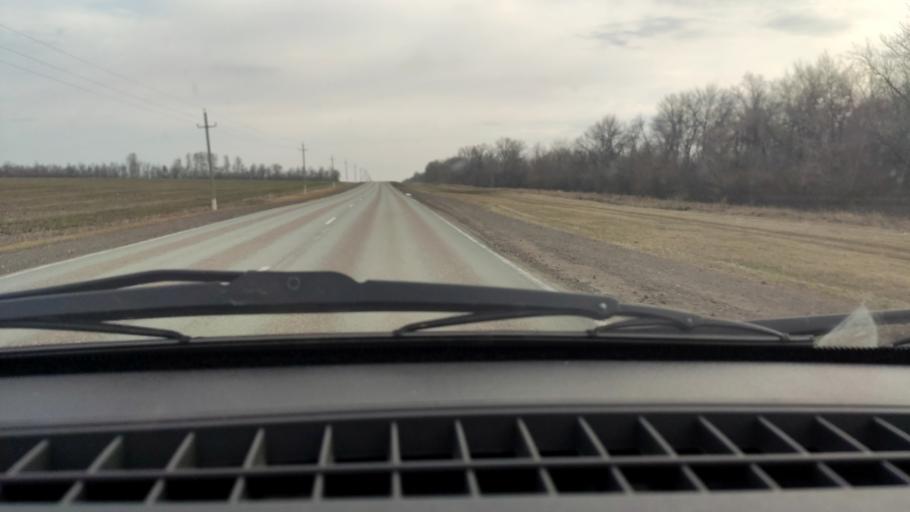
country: RU
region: Bashkortostan
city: Davlekanovo
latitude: 54.3129
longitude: 55.1470
